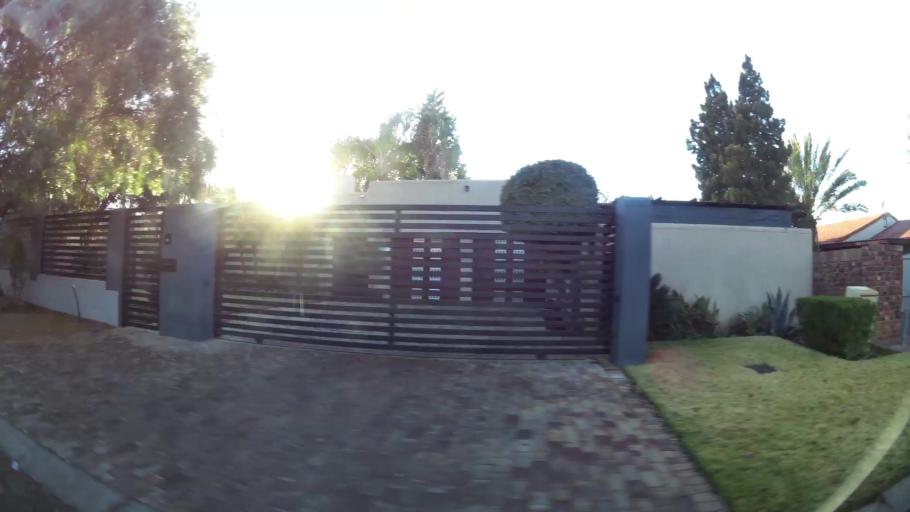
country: ZA
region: Northern Cape
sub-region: Frances Baard District Municipality
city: Kimberley
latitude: -28.7584
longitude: 24.7527
